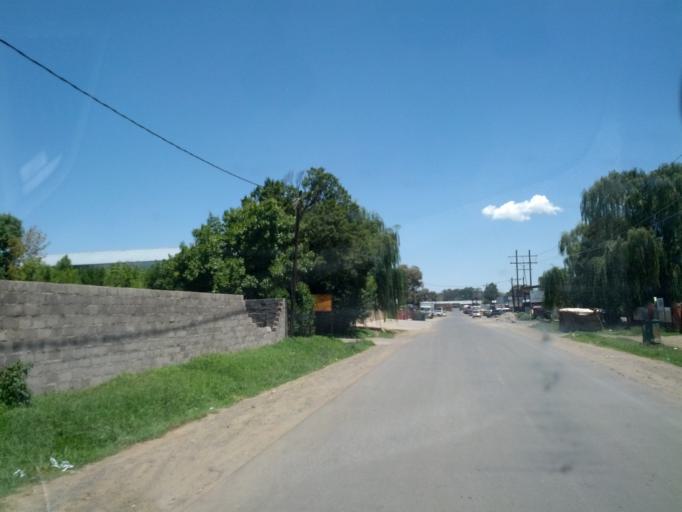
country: LS
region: Maseru
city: Maseru
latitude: -29.2955
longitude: 27.4775
